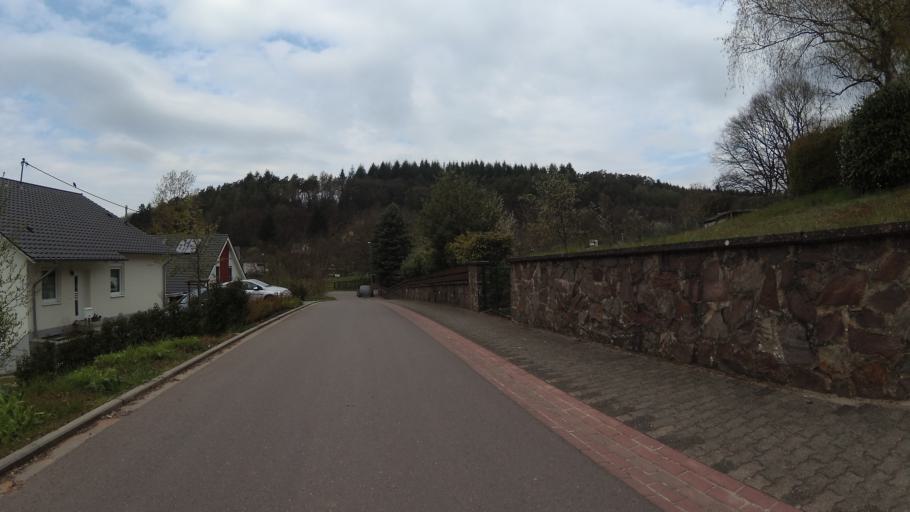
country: DE
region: Saarland
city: Mettlach
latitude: 49.4788
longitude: 6.6050
